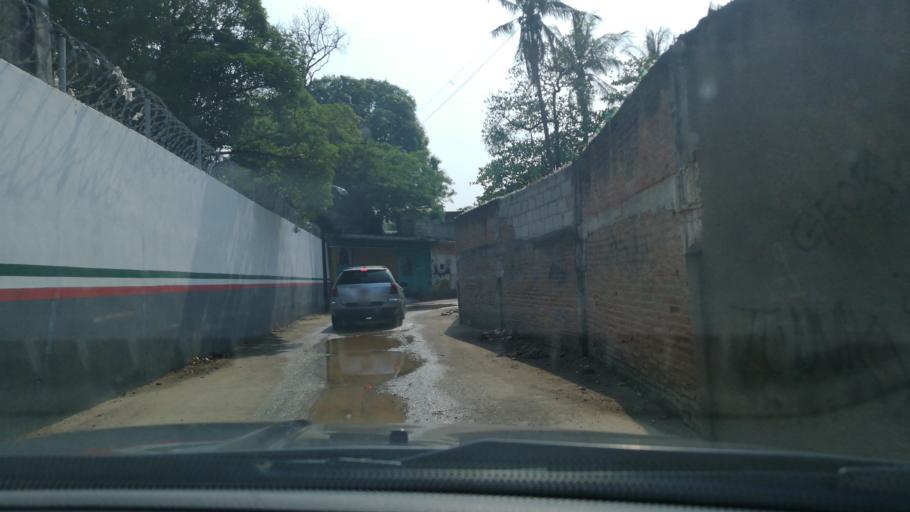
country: MX
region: Oaxaca
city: San Blas Atempa
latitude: 16.3395
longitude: -95.2233
